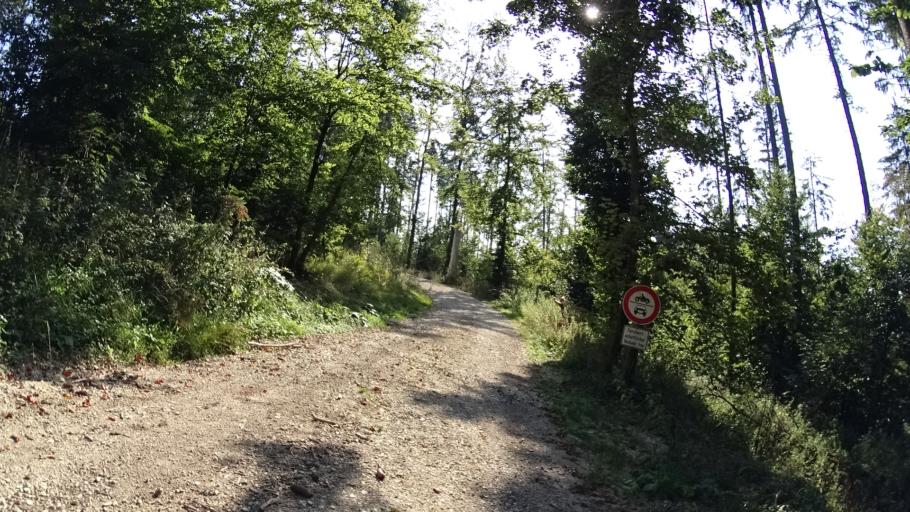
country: DE
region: Bavaria
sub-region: Upper Bavaria
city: Walting
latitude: 48.9310
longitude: 11.2571
